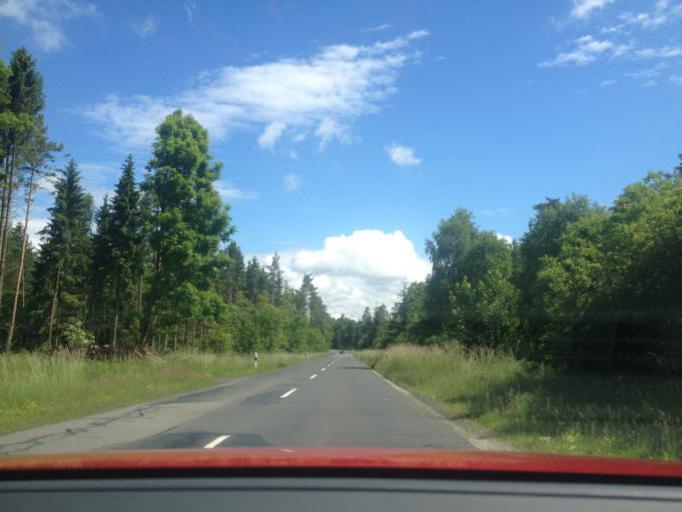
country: DE
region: Bavaria
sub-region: Upper Palatinate
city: Pechbrunn
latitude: 49.9897
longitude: 12.1828
